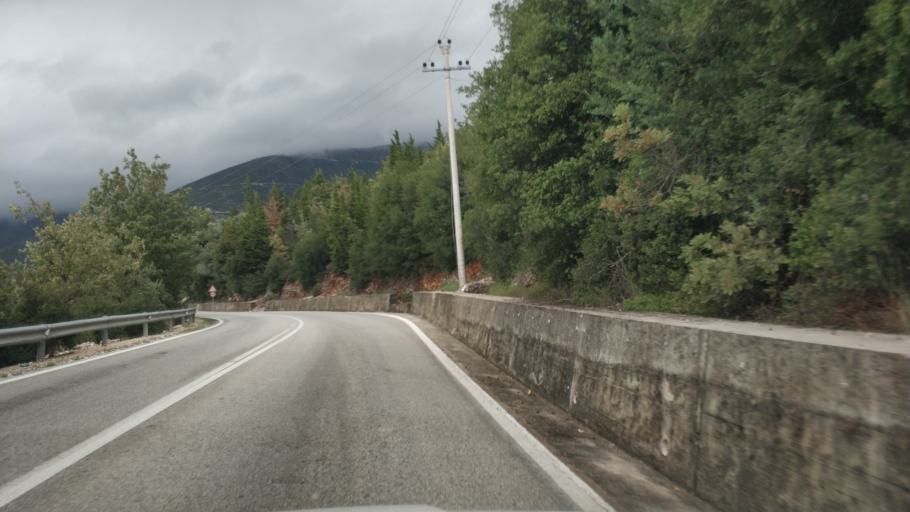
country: AL
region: Vlore
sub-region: Rrethi i Vlores
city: Vranisht
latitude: 40.1688
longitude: 19.6178
